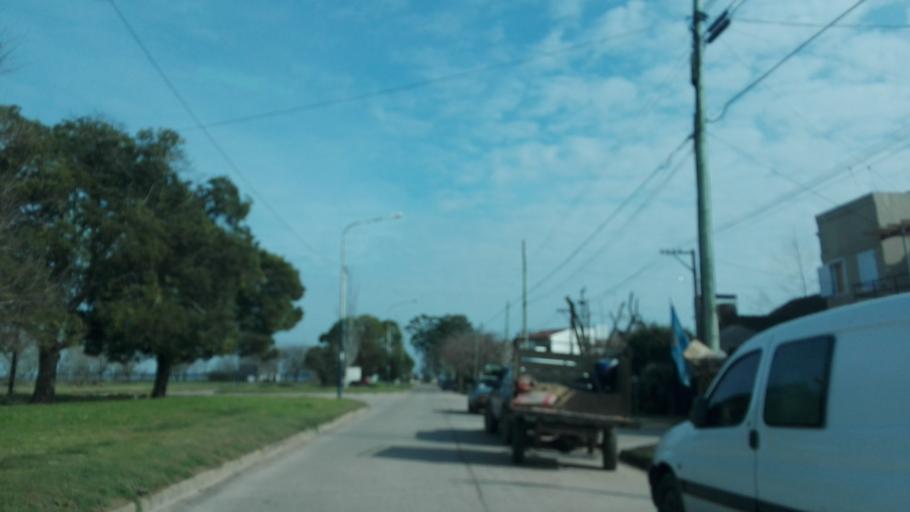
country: AR
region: Buenos Aires
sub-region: Partido de Chascomus
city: Chascomus
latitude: -35.5687
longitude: -58.0223
